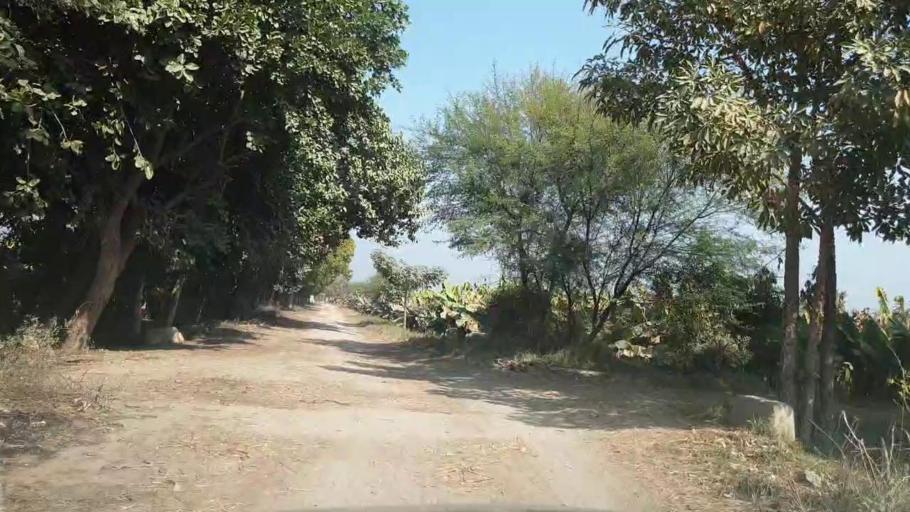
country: PK
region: Sindh
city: Matiari
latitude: 25.5471
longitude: 68.4980
